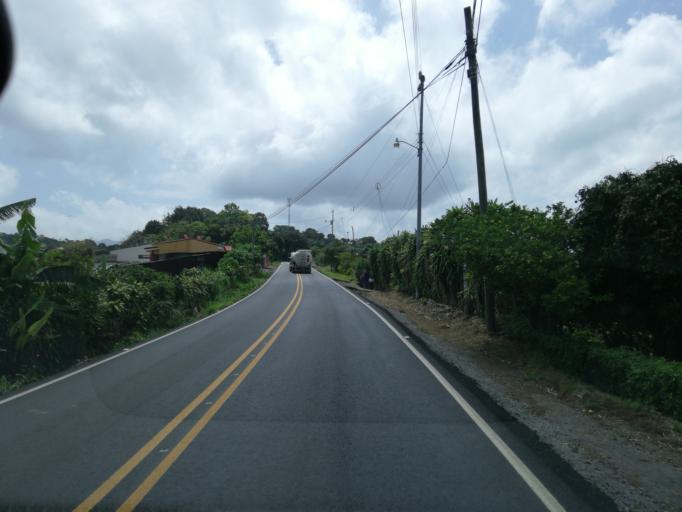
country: CR
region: Alajuela
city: Naranjo
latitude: 10.1305
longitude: -84.4005
